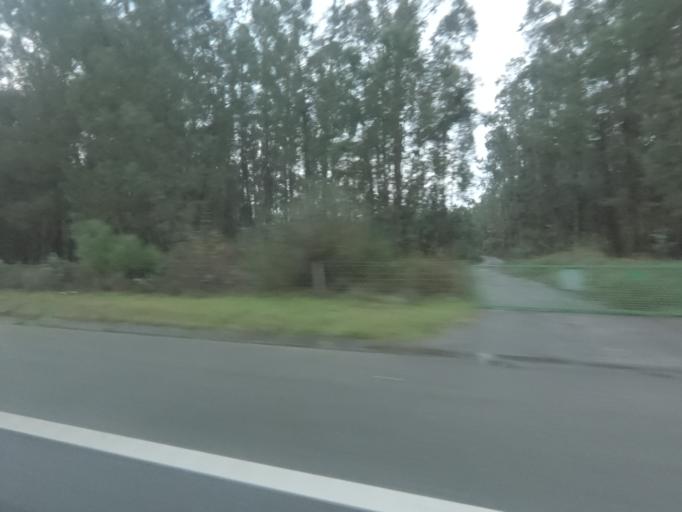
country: PT
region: Braga
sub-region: Barcelos
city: Galegos
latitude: 41.6241
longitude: -8.5572
